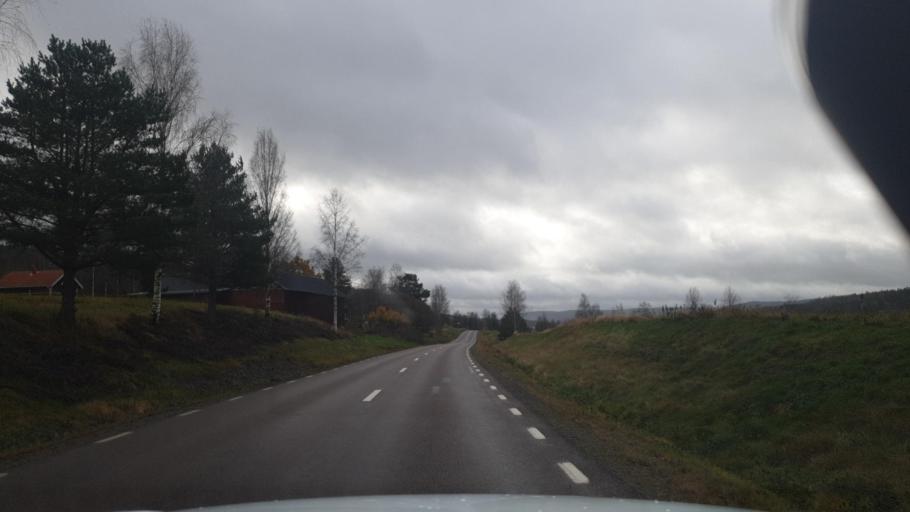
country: SE
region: Vaermland
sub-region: Eda Kommun
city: Amotfors
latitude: 59.6666
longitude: 12.1461
